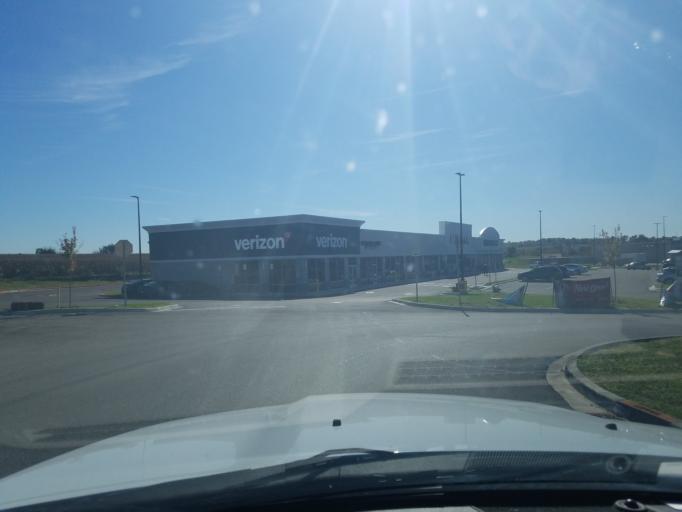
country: US
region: Indiana
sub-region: Washington County
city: Salem
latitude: 38.6152
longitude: -86.0831
